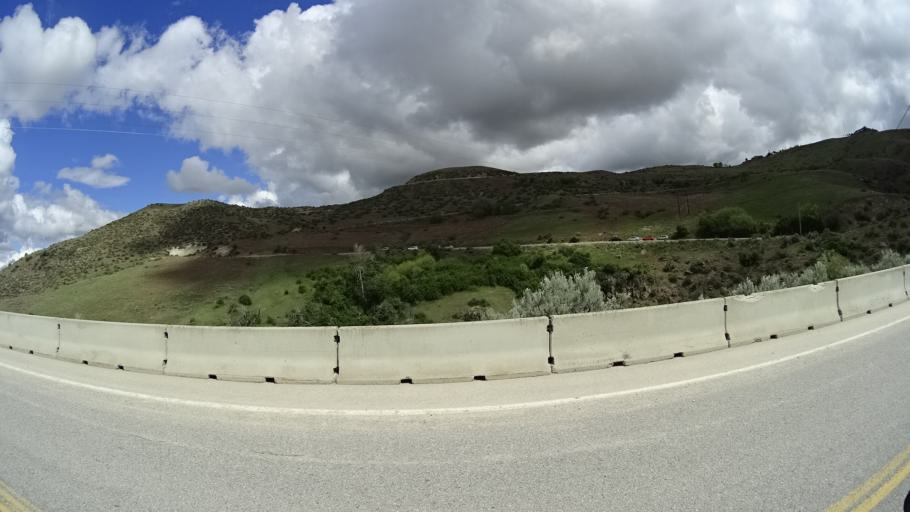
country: US
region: Idaho
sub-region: Ada County
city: Boise
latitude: 43.6868
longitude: -116.1823
